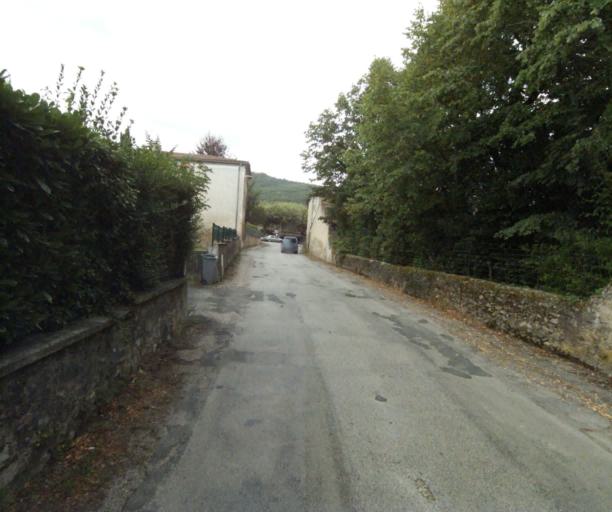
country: FR
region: Midi-Pyrenees
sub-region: Departement du Tarn
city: Soreze
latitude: 43.4540
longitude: 2.0656
